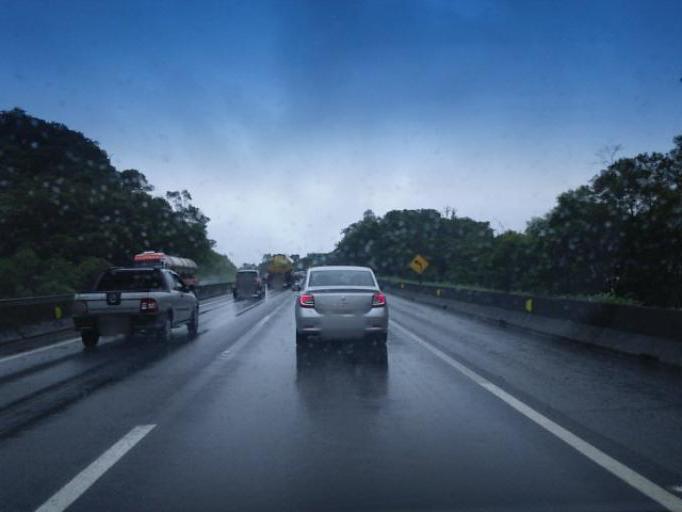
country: BR
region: Santa Catarina
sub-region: Joinville
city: Joinville
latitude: -26.1307
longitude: -48.8925
